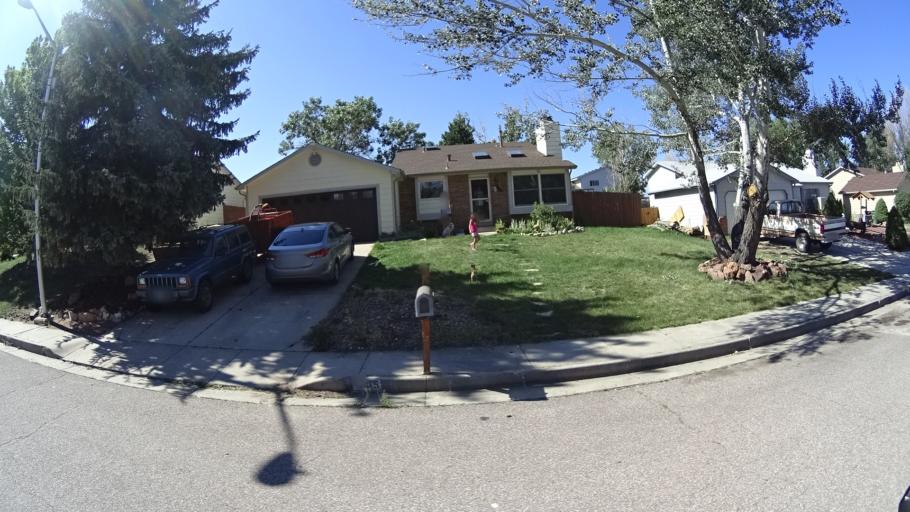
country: US
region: Colorado
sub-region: El Paso County
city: Air Force Academy
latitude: 38.9415
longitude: -104.7899
